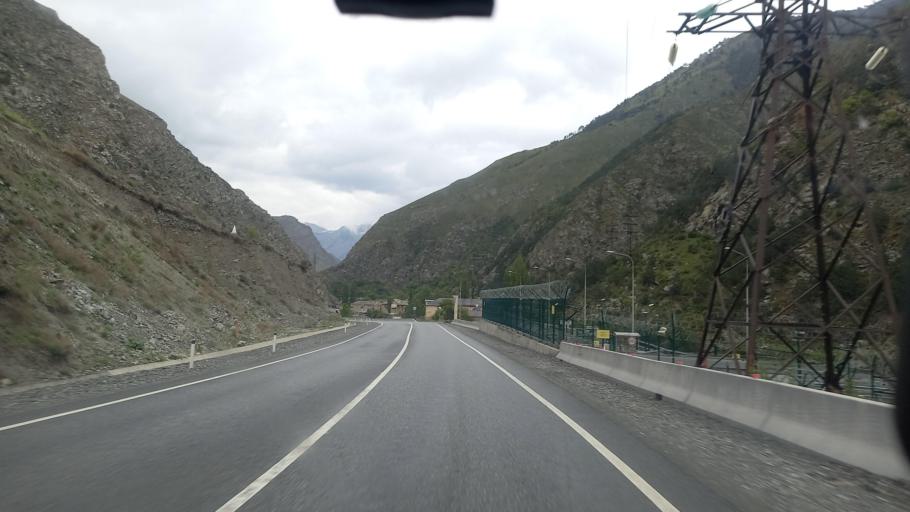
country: RU
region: North Ossetia
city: Mizur
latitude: 42.8462
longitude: 44.0439
